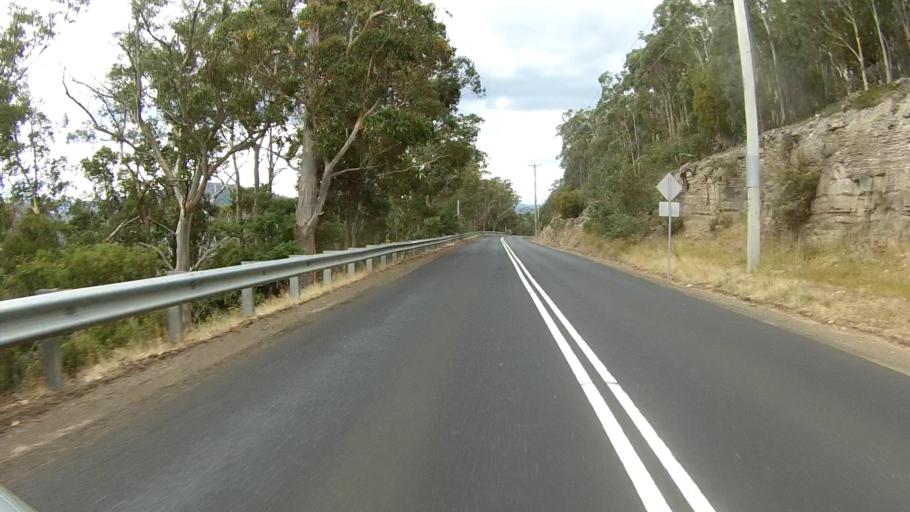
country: AU
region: Tasmania
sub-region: Hobart
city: Dynnyrne
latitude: -42.9062
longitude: 147.2755
